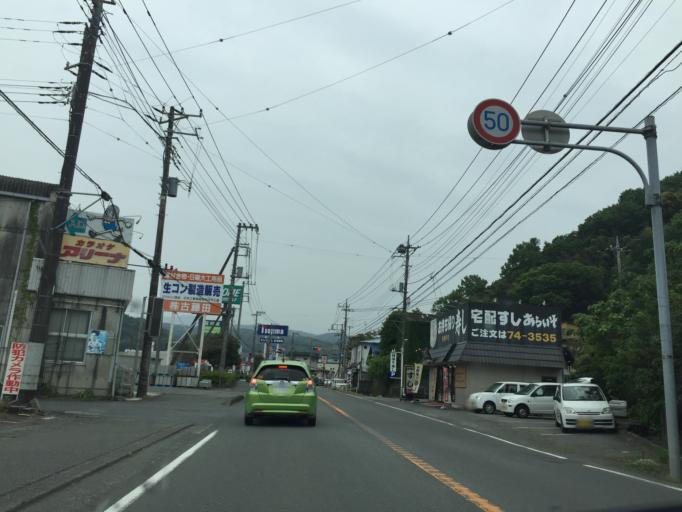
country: JP
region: Shizuoka
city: Mishima
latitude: 34.9875
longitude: 138.9491
